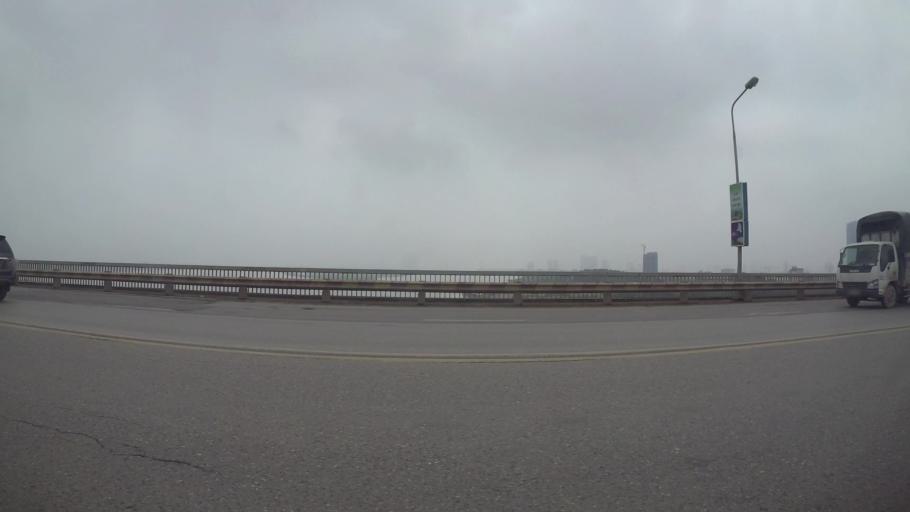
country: VN
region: Ha Noi
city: Tay Ho
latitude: 21.0944
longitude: 105.7861
